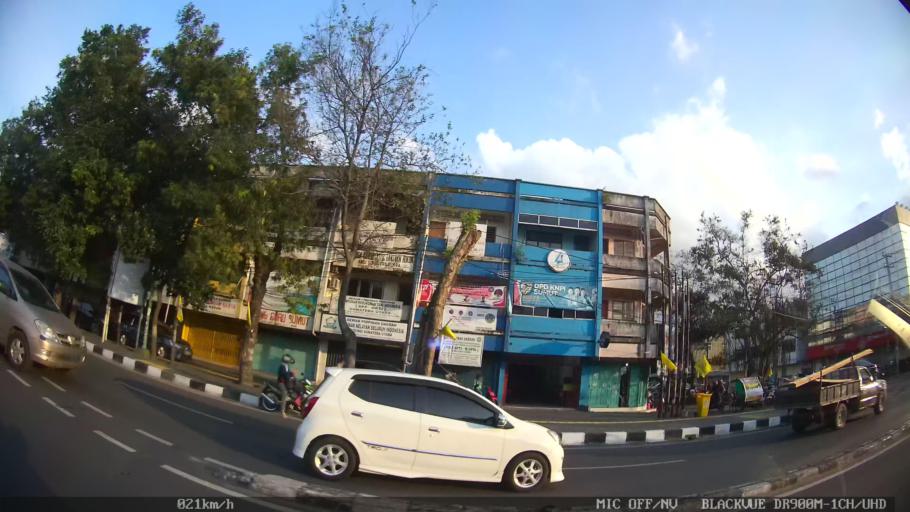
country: ID
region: North Sumatra
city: Medan
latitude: 3.5919
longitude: 98.6655
